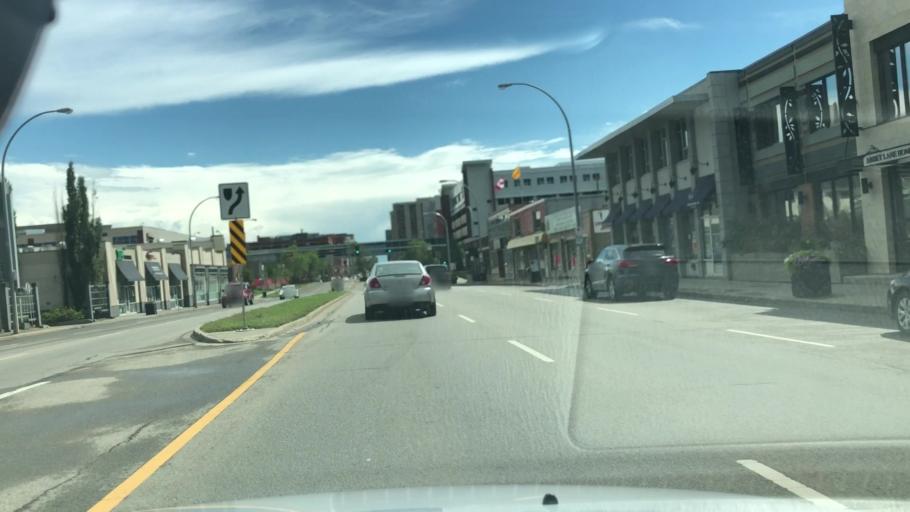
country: CA
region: Alberta
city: Edmonton
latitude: 53.5494
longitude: -113.5085
